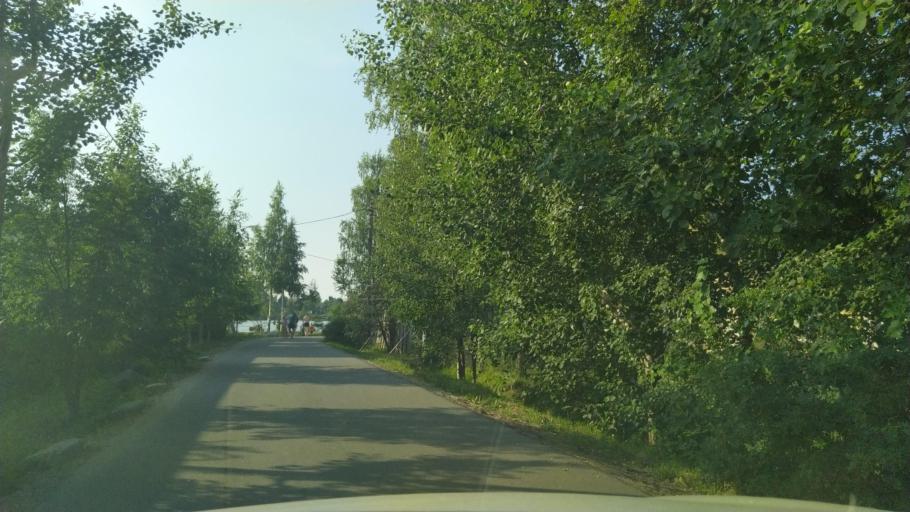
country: RU
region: Leningrad
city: Koltushi
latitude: 59.8915
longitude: 30.7318
